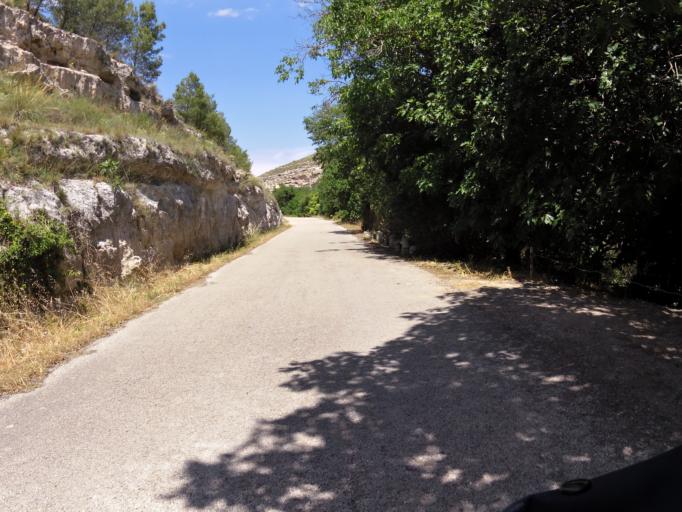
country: ES
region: Castille-La Mancha
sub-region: Provincia de Albacete
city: Jorquera
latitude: 39.1703
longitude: -1.5337
